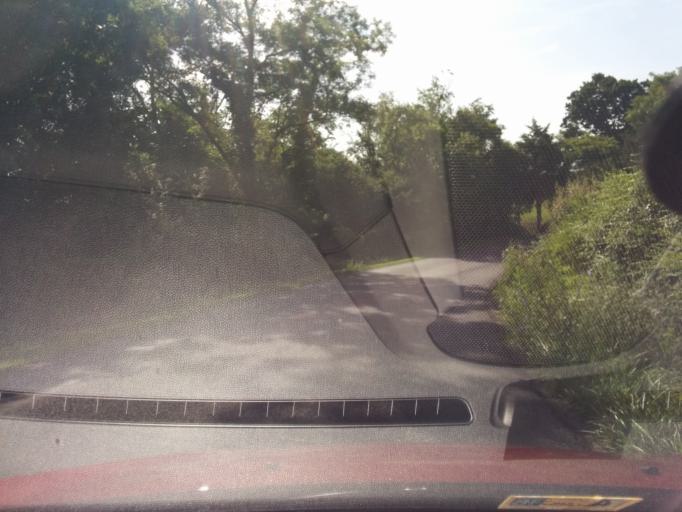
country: US
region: Virginia
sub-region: City of Lexington
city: Lexington
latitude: 37.7738
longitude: -79.4762
